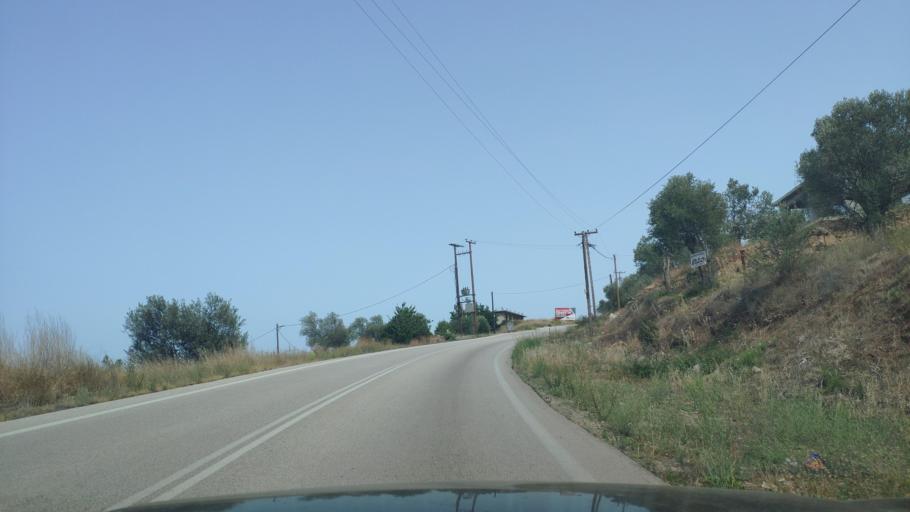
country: GR
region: Peloponnese
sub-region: Nomos Argolidos
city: Palaia Epidavros
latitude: 37.6312
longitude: 23.1381
